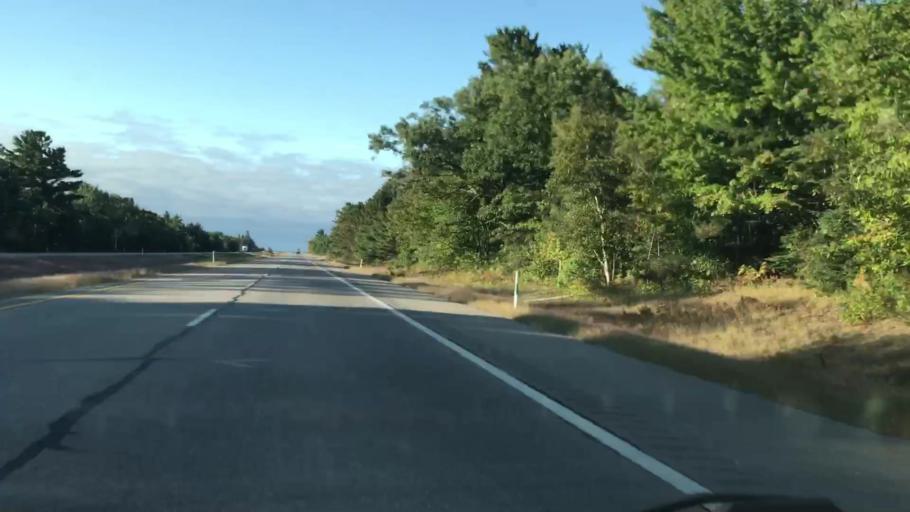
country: US
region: Michigan
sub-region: Chippewa County
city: Sault Ste. Marie
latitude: 46.4338
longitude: -84.3896
